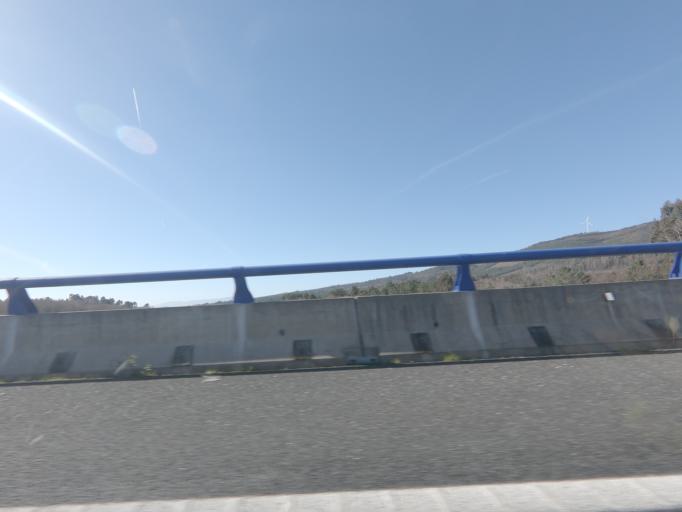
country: ES
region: Galicia
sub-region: Provincia de Ourense
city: Pinor
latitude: 42.4956
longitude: -8.0275
